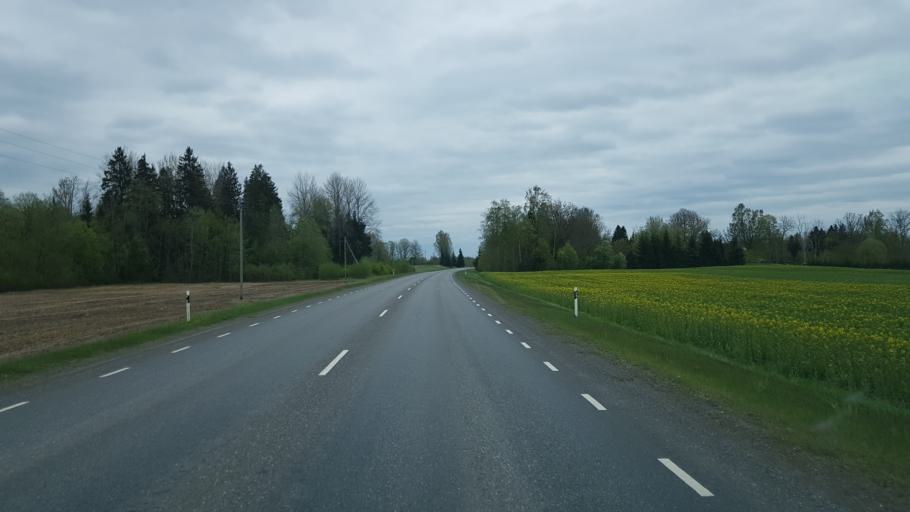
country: EE
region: Viljandimaa
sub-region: Viljandi linn
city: Viljandi
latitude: 58.4505
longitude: 25.5954
